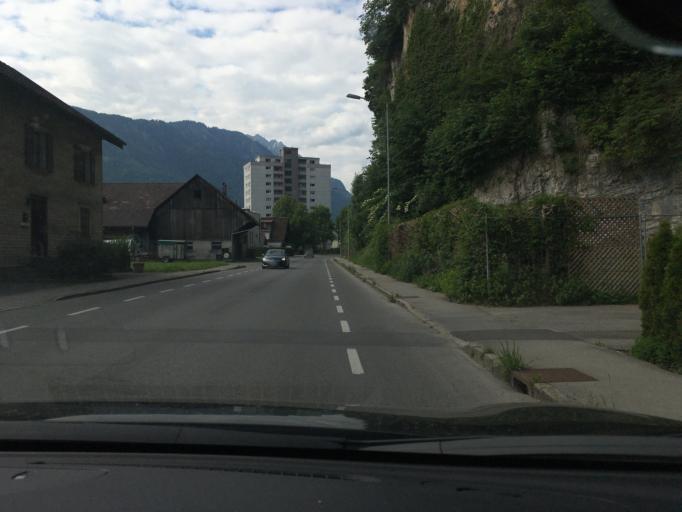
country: AT
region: Vorarlberg
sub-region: Politischer Bezirk Feldkirch
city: Nofels
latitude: 47.2442
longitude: 9.5825
